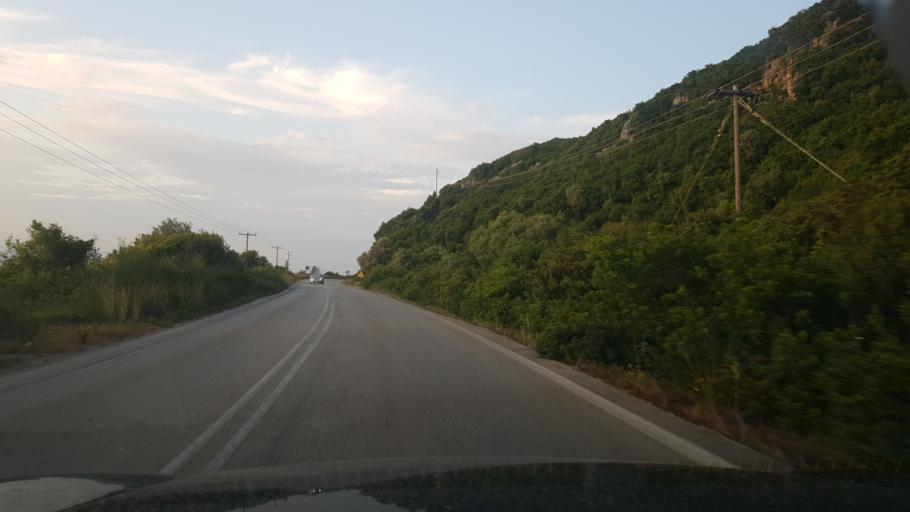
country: GR
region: Ionian Islands
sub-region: Lefkada
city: Lefkada
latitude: 38.8534
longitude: 20.7478
